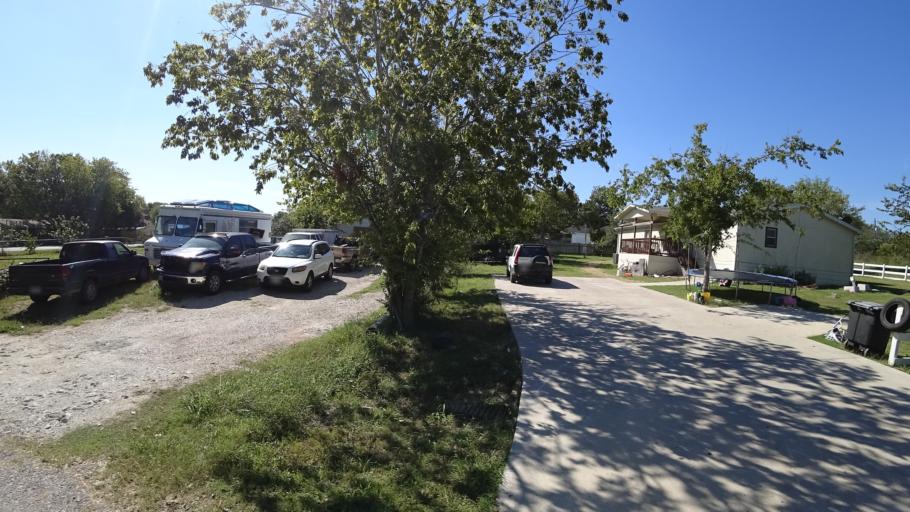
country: US
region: Texas
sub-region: Travis County
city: Hornsby Bend
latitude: 30.2767
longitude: -97.6227
